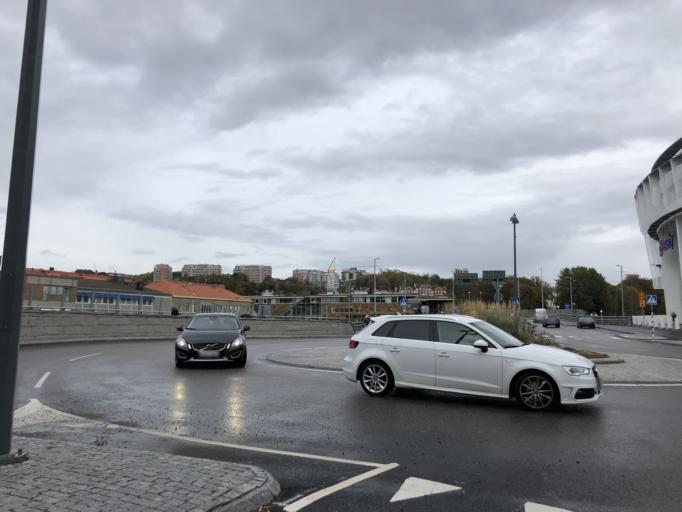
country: SE
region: Vaestra Goetaland
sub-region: Molndal
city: Moelndal
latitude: 57.6547
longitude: 12.0153
